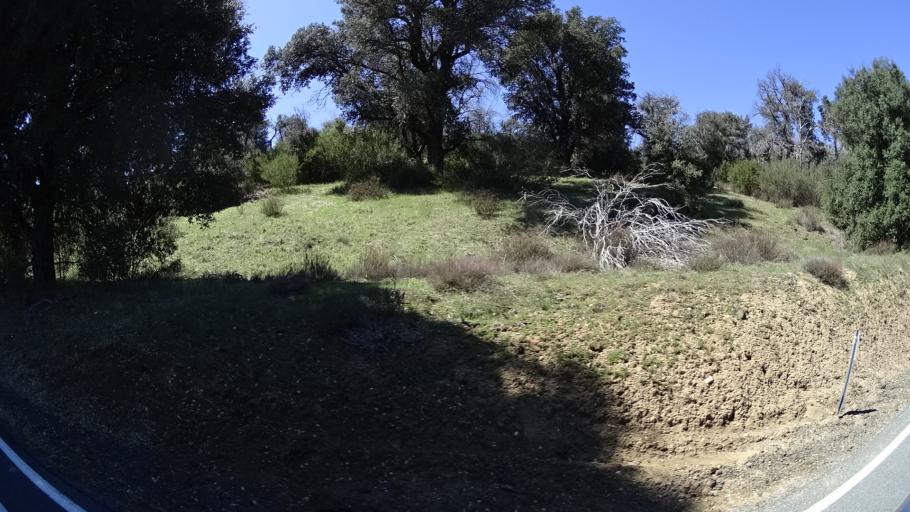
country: US
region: California
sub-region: San Diego County
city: Descanso
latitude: 32.9164
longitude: -116.5716
